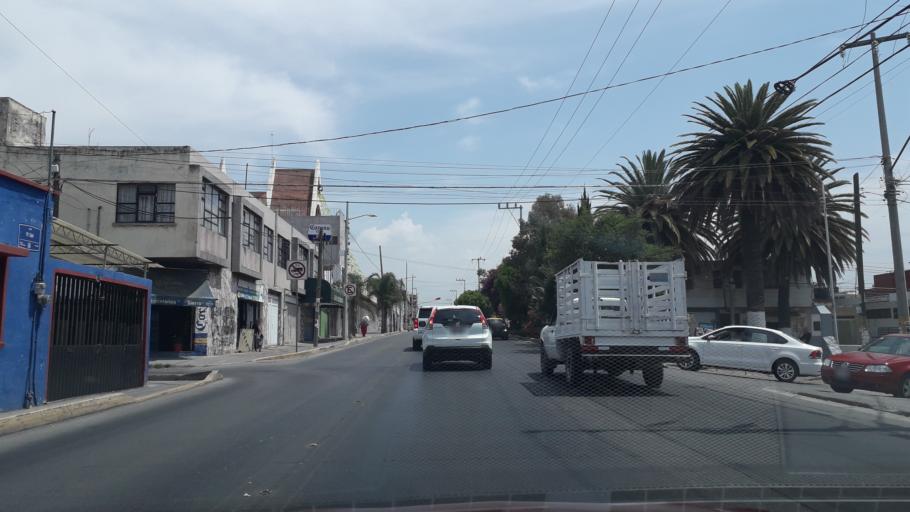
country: MX
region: Puebla
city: Puebla
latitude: 19.0192
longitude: -98.2283
